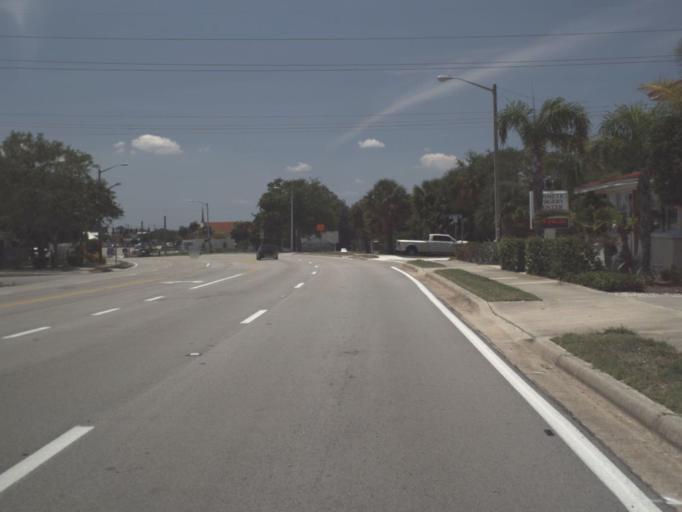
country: US
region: Florida
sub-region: Brevard County
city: Melbourne
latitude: 28.0795
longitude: -80.6141
